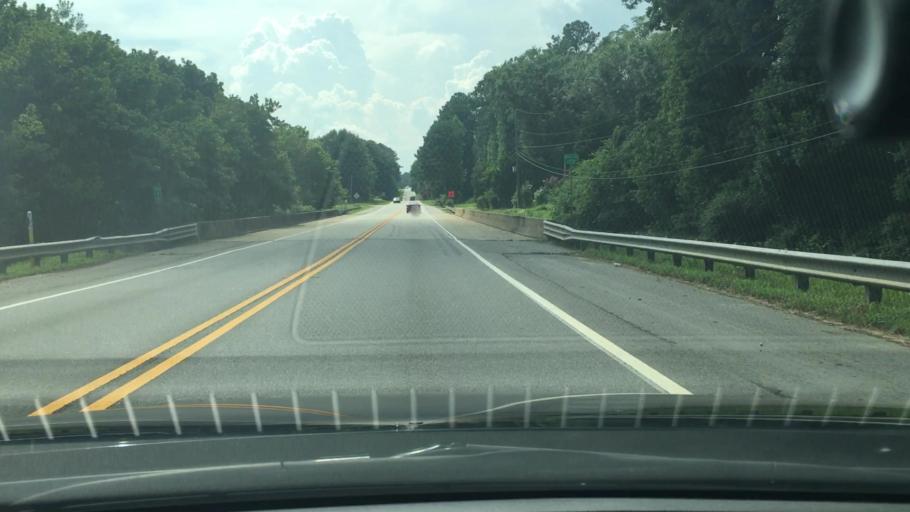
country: US
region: Georgia
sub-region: Coweta County
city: East Newnan
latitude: 33.3332
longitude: -84.7102
